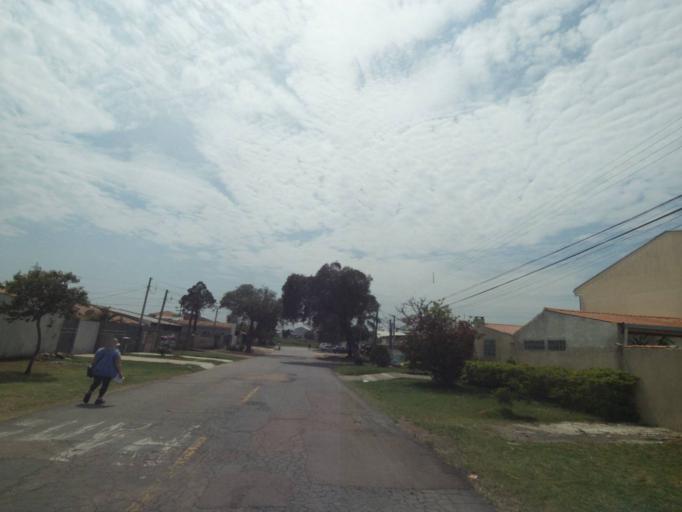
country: BR
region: Parana
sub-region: Pinhais
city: Pinhais
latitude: -25.4241
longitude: -49.1995
